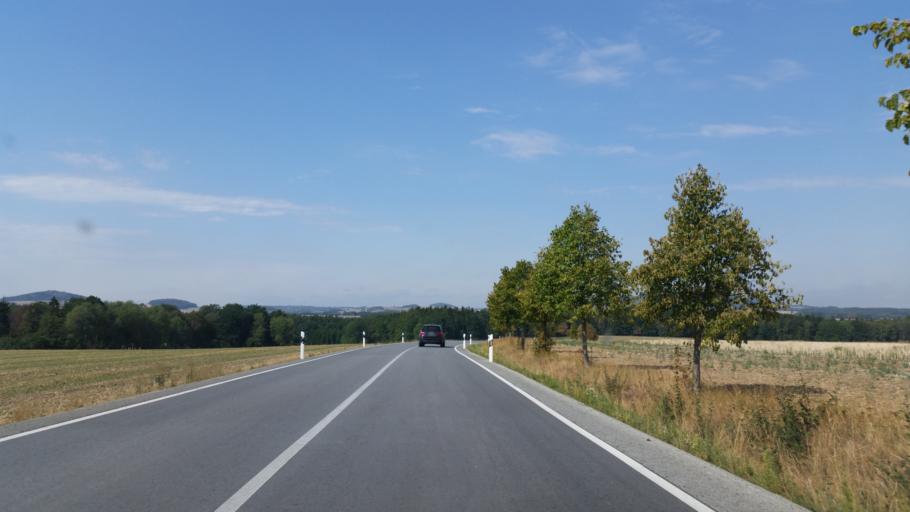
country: DE
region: Saxony
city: Grosshennersdorf
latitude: 50.9805
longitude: 14.7670
